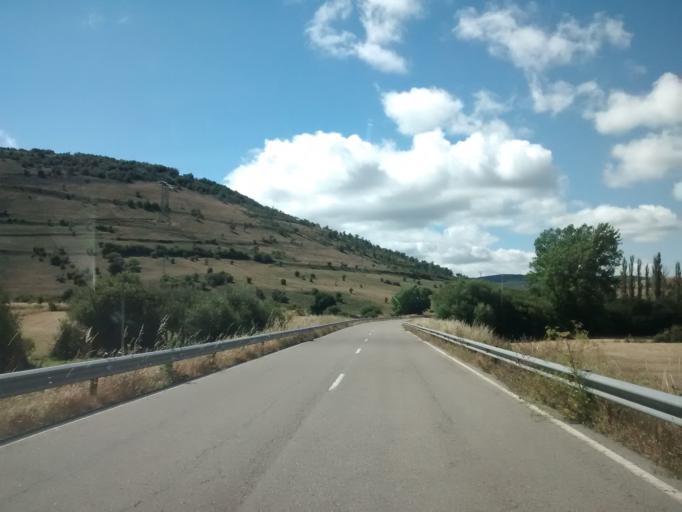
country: ES
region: Cantabria
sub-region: Provincia de Cantabria
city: Mataporquera
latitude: 42.8993
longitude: -4.0788
